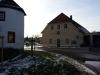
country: DE
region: Thuringia
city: Windischleuba
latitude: 51.0165
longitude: 12.4724
